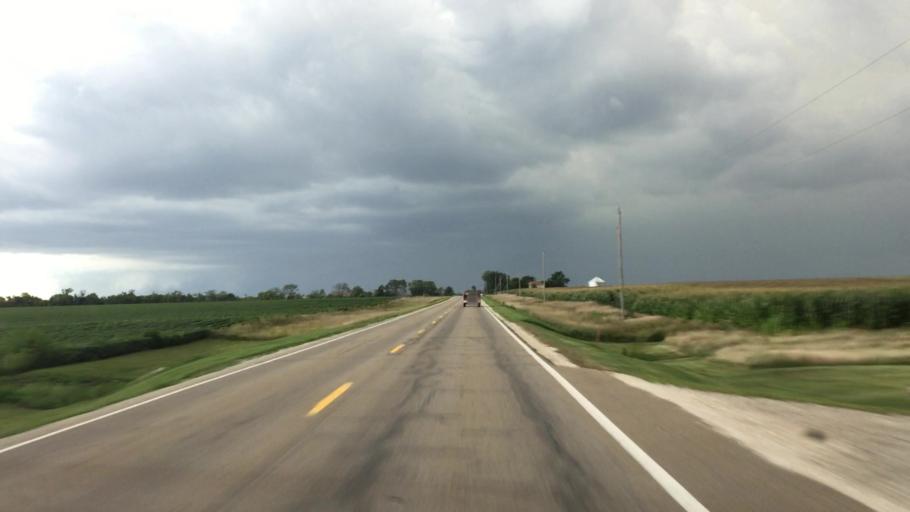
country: US
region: Iowa
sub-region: Henry County
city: New London
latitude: 40.7843
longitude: -91.4988
